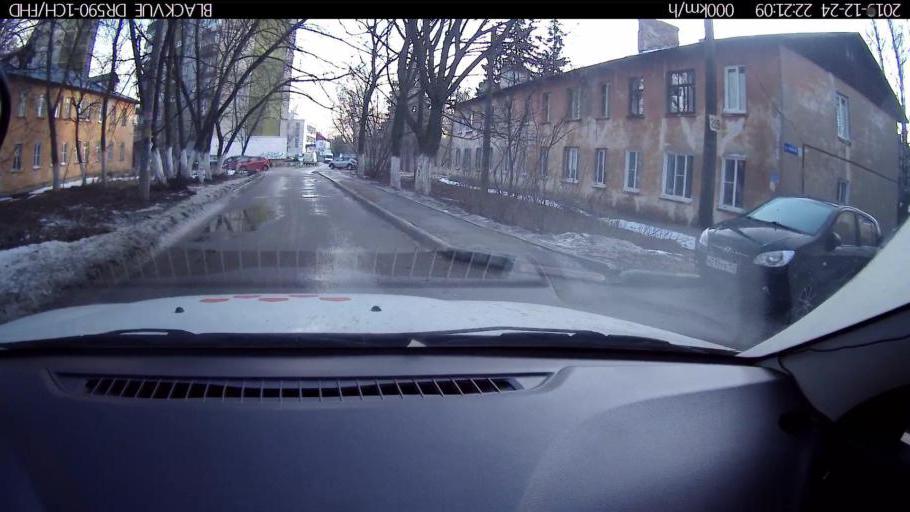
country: RU
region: Nizjnij Novgorod
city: Nizhniy Novgorod
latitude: 56.2375
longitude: 43.9702
